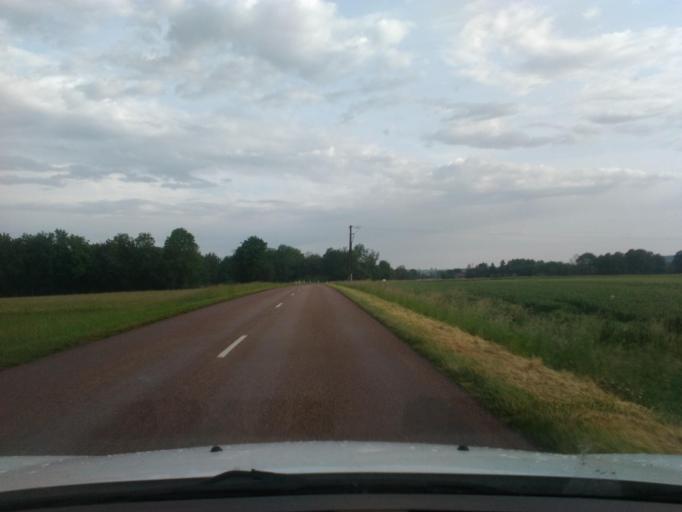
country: FR
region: Lorraine
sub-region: Departement des Vosges
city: Rambervillers
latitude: 48.4246
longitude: 6.5810
